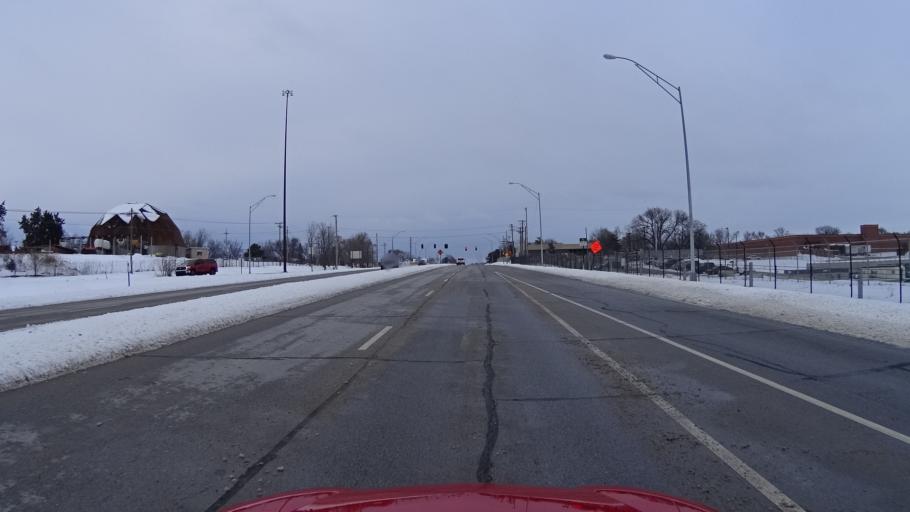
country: US
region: Nebraska
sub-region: Sarpy County
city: Offutt Air Force Base
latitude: 41.1167
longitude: -95.9265
